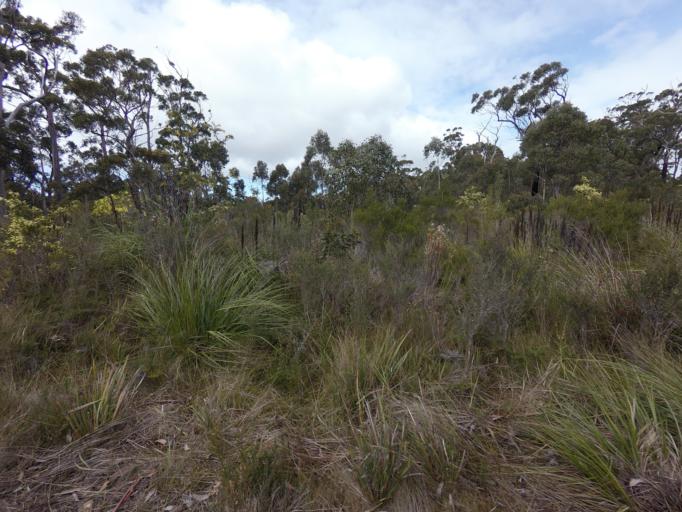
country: AU
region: Tasmania
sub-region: Huon Valley
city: Geeveston
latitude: -43.4802
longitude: 146.9374
